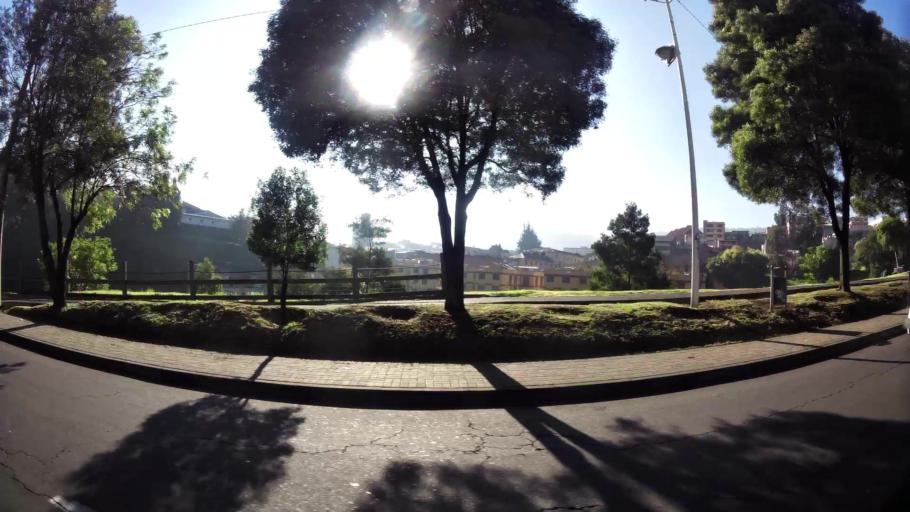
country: EC
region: Pichincha
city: Quito
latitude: -0.2393
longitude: -78.5187
